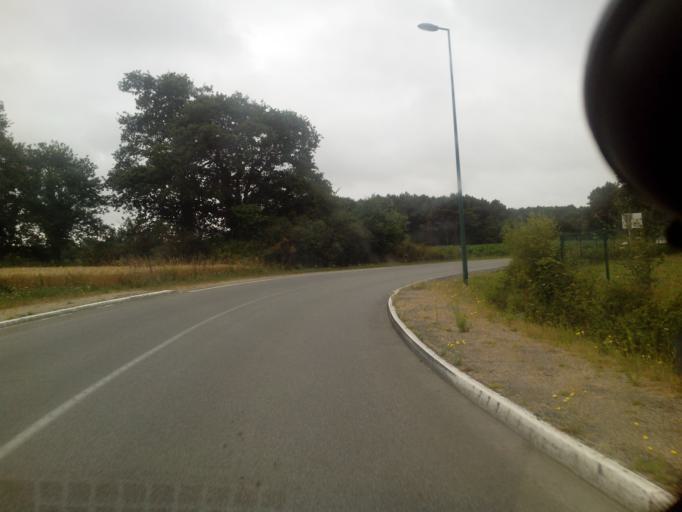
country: FR
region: Brittany
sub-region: Departement du Morbihan
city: Merlevenez
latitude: 47.7295
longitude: -3.2559
